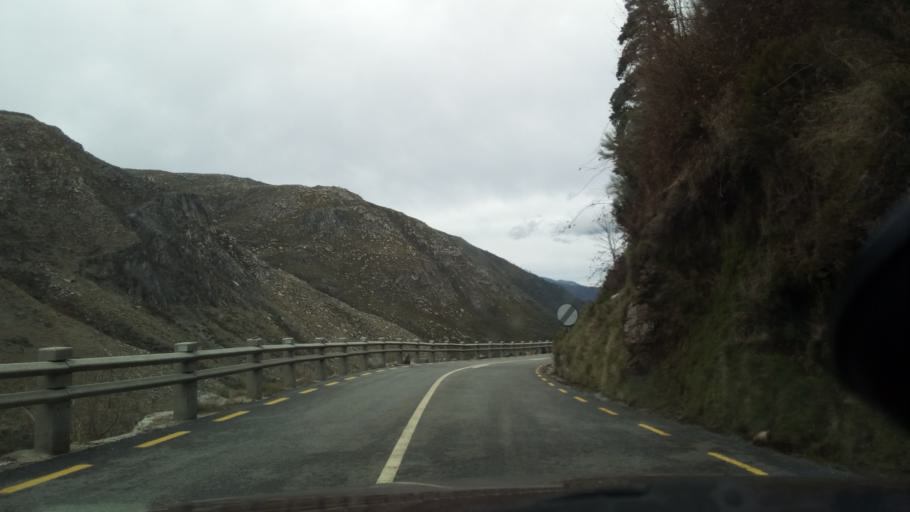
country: PT
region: Guarda
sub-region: Manteigas
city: Manteigas
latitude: 40.3443
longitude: -7.5626
